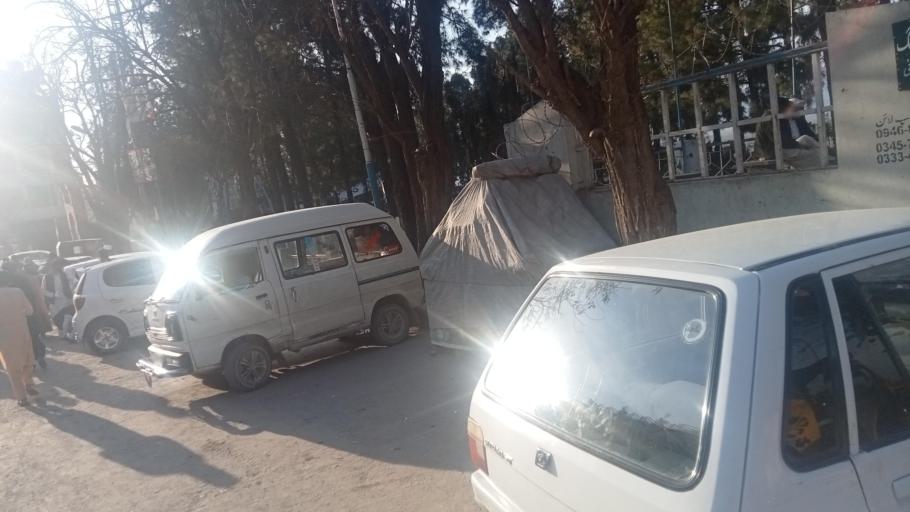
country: PK
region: Khyber Pakhtunkhwa
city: Mingora
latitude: 34.7920
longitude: 72.3792
